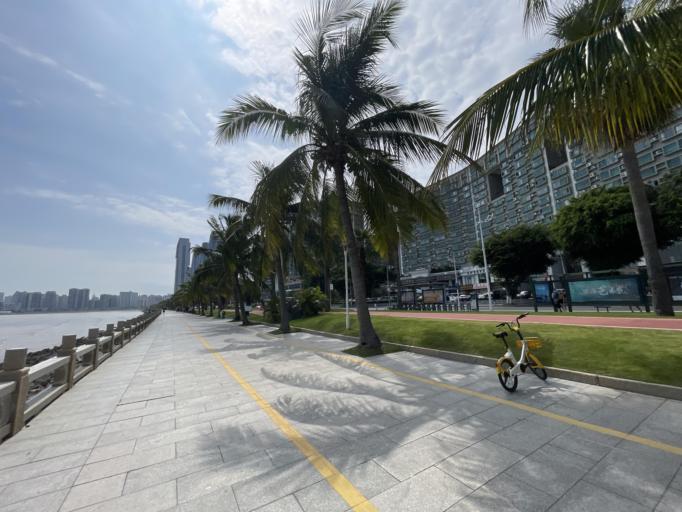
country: CN
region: Guangdong
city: Jida
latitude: 22.2291
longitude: 113.5588
